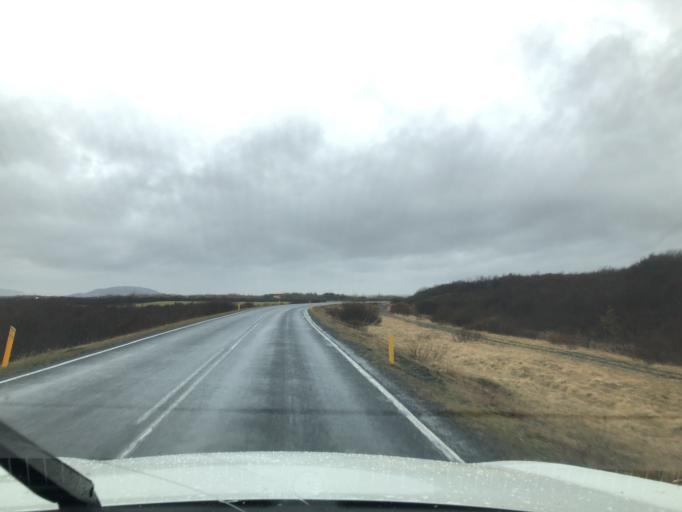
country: IS
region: South
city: Selfoss
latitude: 64.2283
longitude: -20.5694
